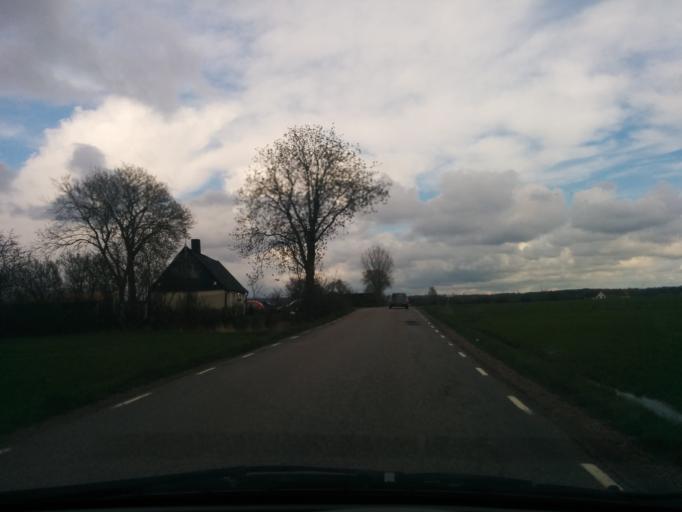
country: SE
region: Skane
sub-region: Lunds Kommun
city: Genarp
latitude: 55.6128
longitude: 13.3501
